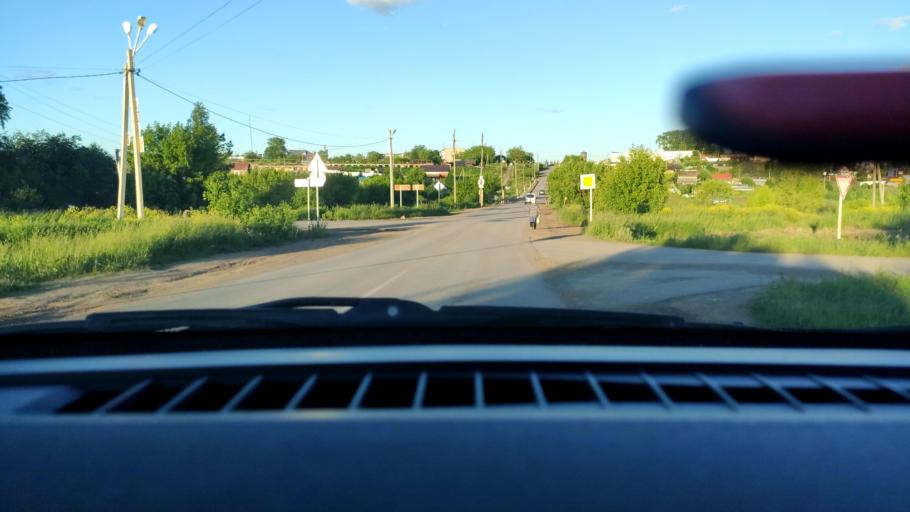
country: RU
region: Perm
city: Kultayevo
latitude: 57.9278
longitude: 55.8765
